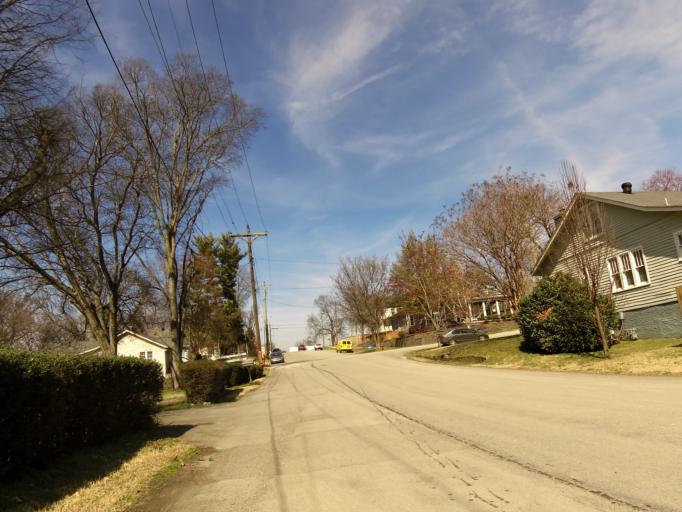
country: US
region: Tennessee
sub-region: Davidson County
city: Belle Meade
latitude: 36.1494
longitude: -86.8471
